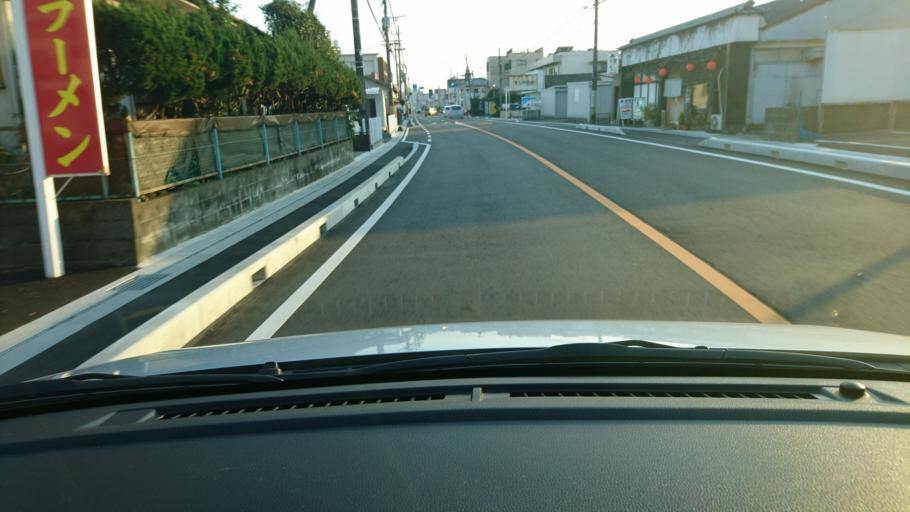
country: JP
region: Miyazaki
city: Miyazaki-shi
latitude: 31.9496
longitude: 131.4328
